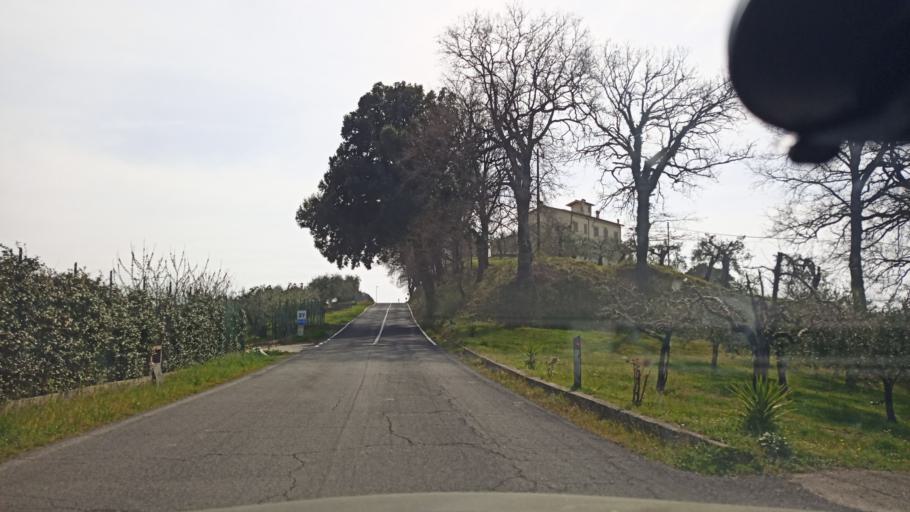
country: IT
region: Latium
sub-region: Provincia di Rieti
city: Torri in Sabina
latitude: 42.3455
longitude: 12.6507
